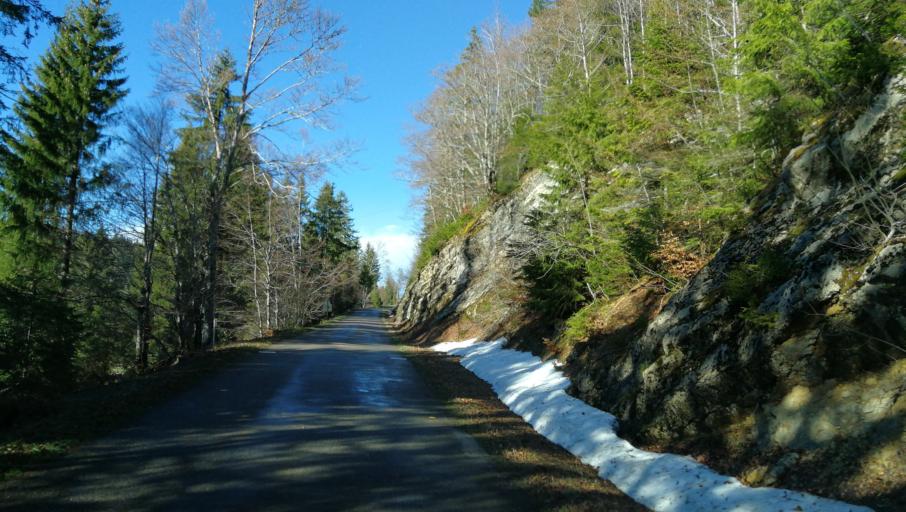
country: FR
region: Franche-Comte
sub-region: Departement du Jura
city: Saint-Claude
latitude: 46.3045
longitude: 5.8992
